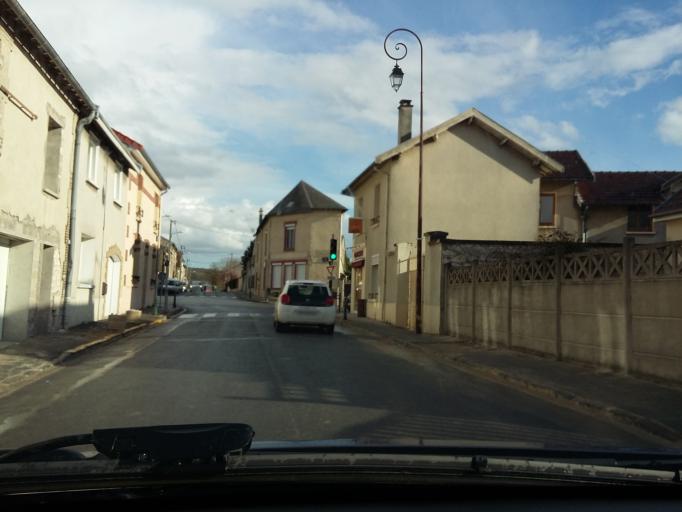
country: FR
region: Champagne-Ardenne
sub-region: Departement de la Marne
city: Cernay-les-Reims
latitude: 49.2632
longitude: 4.1048
